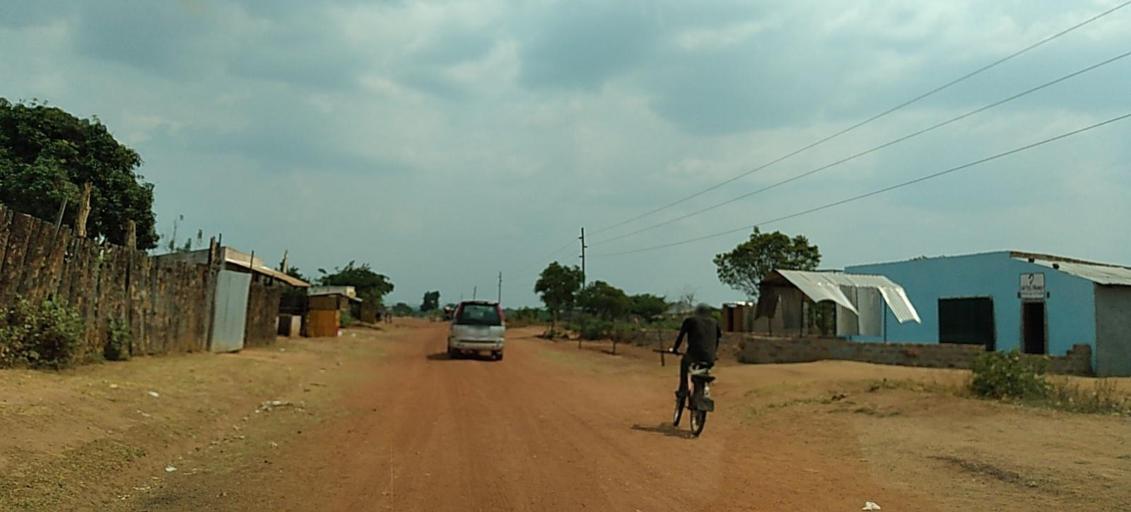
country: ZM
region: Copperbelt
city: Kalulushi
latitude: -12.8645
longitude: 28.0779
